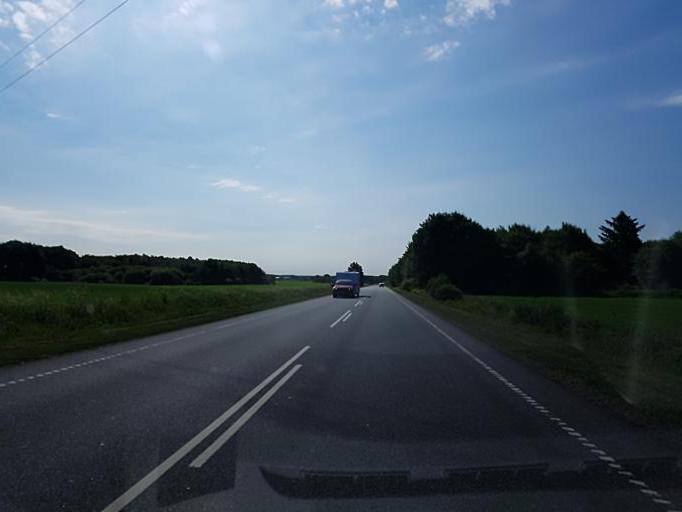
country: DK
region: South Denmark
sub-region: Esbjerg Kommune
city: Tjaereborg
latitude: 55.5049
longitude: 8.6024
